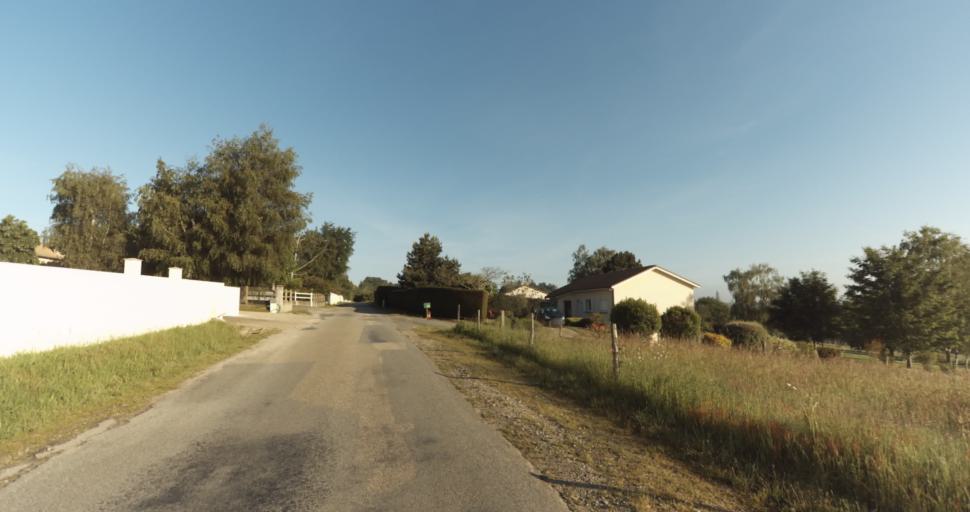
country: FR
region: Limousin
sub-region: Departement de la Haute-Vienne
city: Condat-sur-Vienne
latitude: 45.7801
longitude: 1.2944
